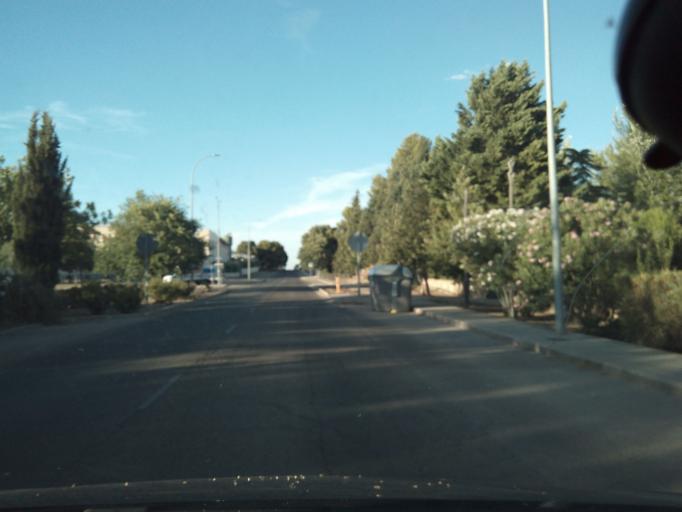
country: ES
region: Castille-La Mancha
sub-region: Province of Toledo
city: Villacanas
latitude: 39.6119
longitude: -3.3446
